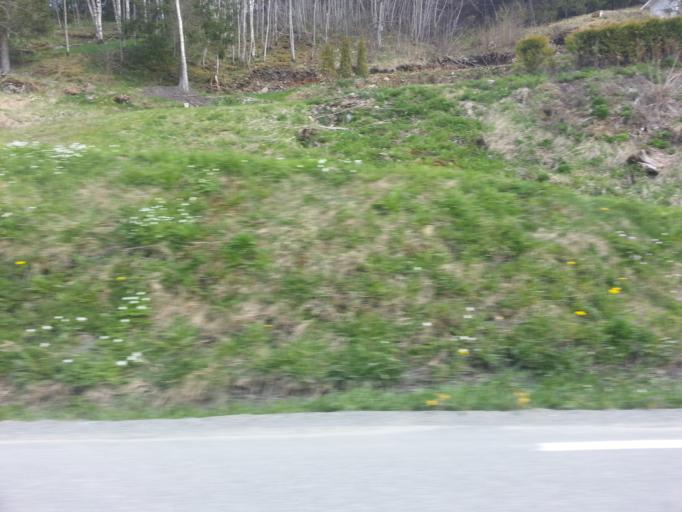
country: NO
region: Nord-Trondelag
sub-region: Levanger
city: Skogn
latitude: 63.6415
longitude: 11.2568
